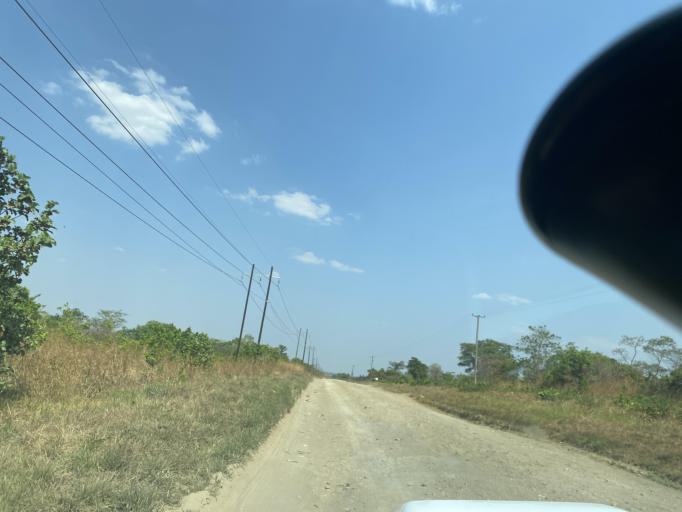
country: ZM
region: Lusaka
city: Lusaka
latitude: -15.3102
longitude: 28.0476
